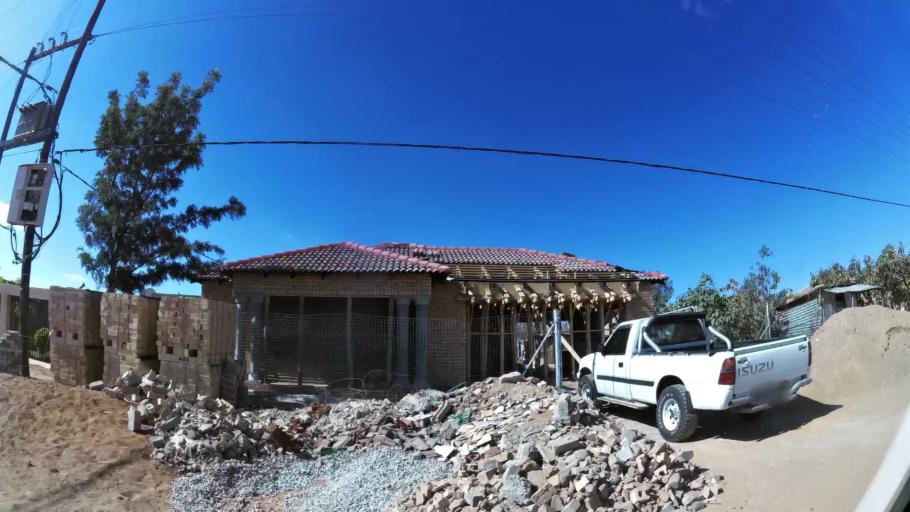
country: ZA
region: Limpopo
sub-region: Capricorn District Municipality
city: Polokwane
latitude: -23.8825
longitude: 29.4032
